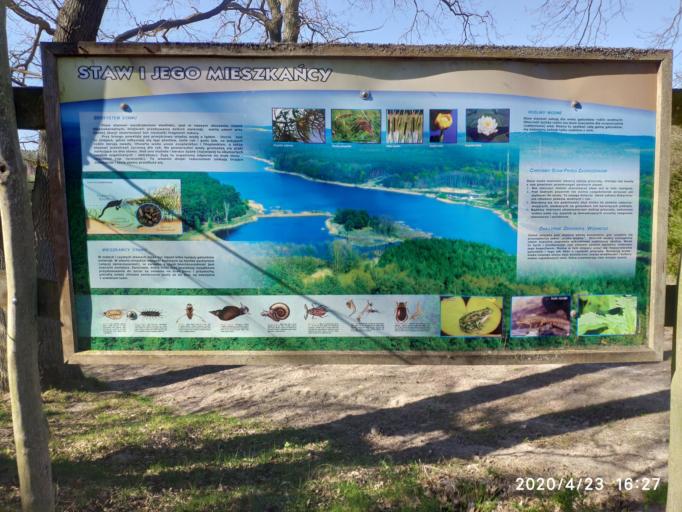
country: PL
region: Lubusz
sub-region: Powiat slubicki
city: Osno Lubuskie
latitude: 52.4714
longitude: 14.8798
